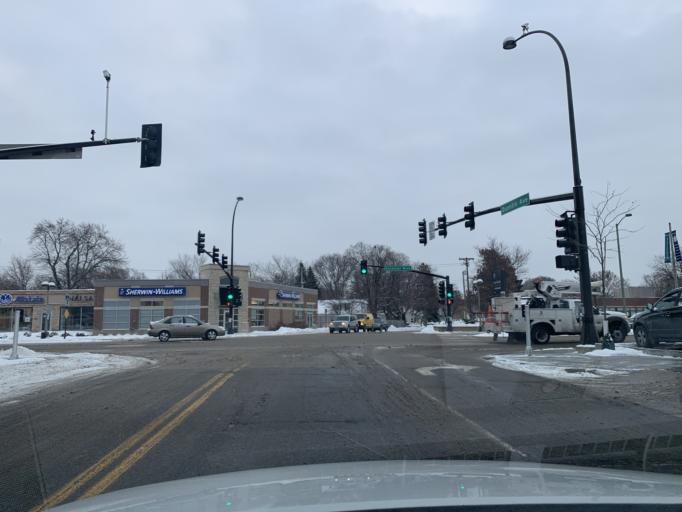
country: US
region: Minnesota
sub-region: Hennepin County
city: Saint Louis Park
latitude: 44.9326
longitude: -93.3435
